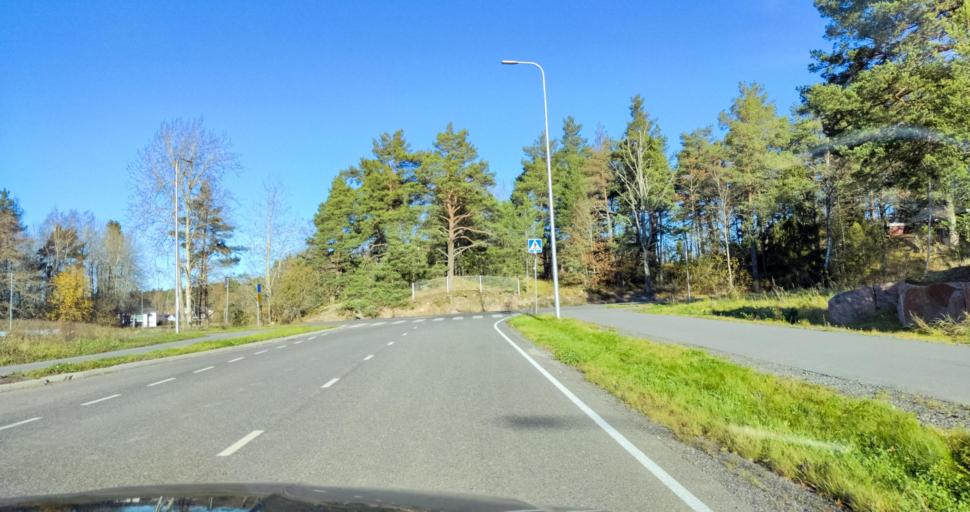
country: FI
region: Varsinais-Suomi
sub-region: Turku
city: Turku
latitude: 60.4074
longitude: 22.2080
